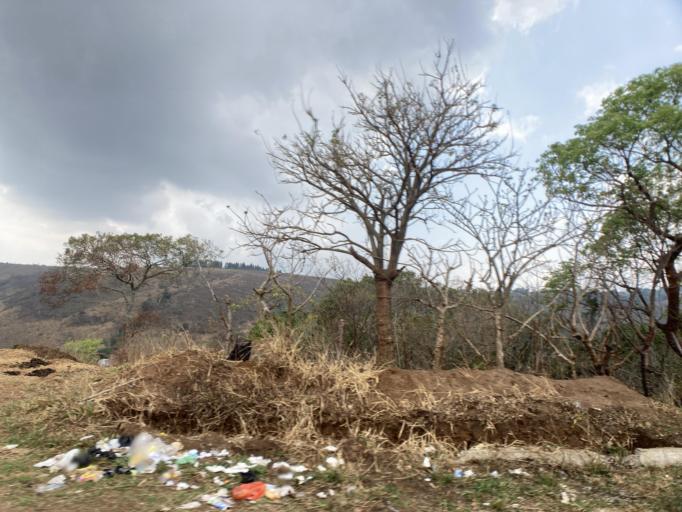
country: GT
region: Escuintla
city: San Vicente Pacaya
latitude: 14.3302
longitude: -90.5648
